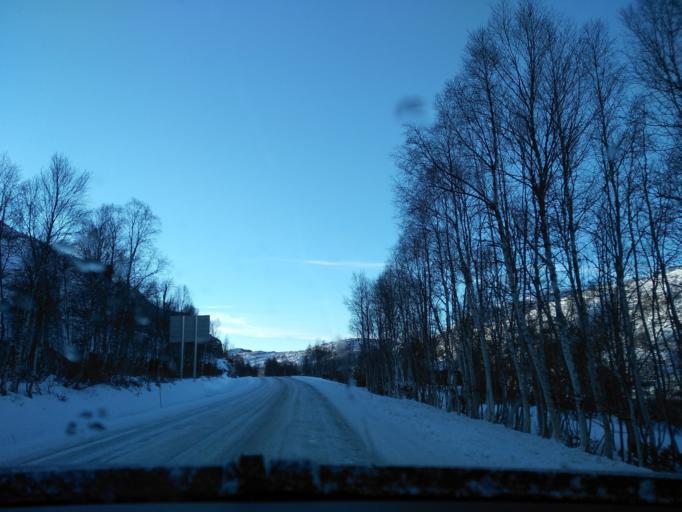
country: NO
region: Vest-Agder
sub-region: Sirdal
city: Tonstad
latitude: 59.0113
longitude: 6.9367
